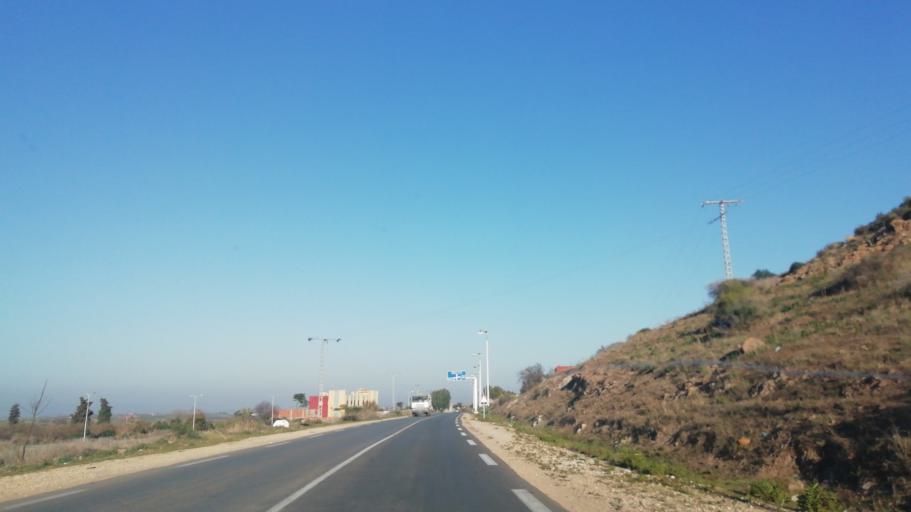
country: MA
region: Oriental
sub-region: Berkane-Taourirt
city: Ahfir
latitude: 34.9673
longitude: -2.0987
